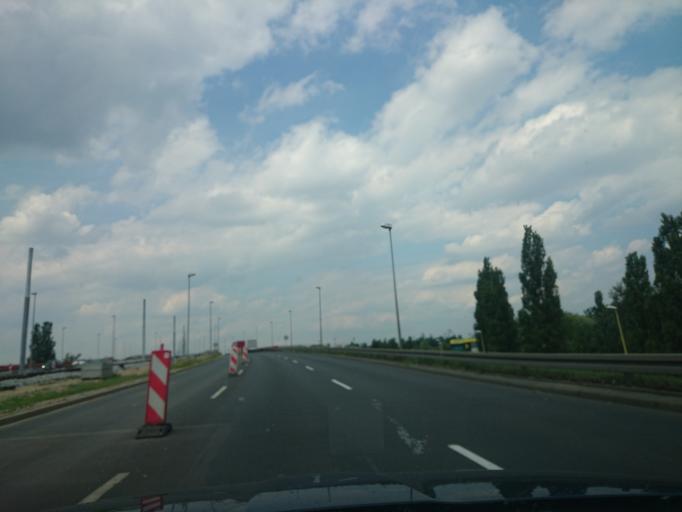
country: PL
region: West Pomeranian Voivodeship
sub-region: Szczecin
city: Szczecin
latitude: 53.3922
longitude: 14.6171
